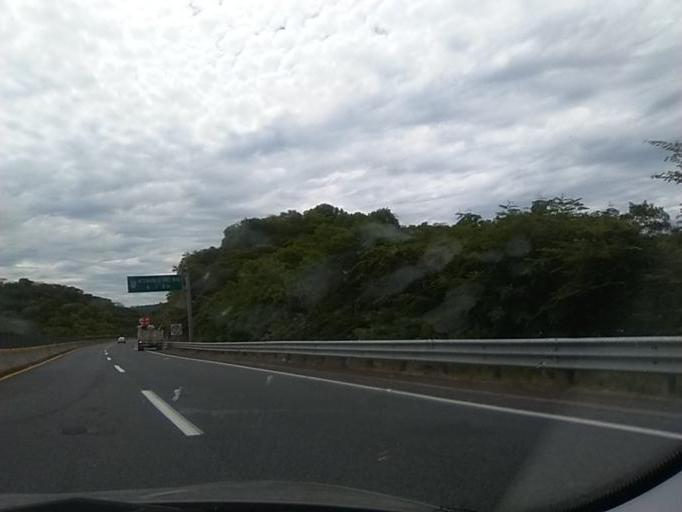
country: MX
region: Guerrero
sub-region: Huitzuco de los Figueroa
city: Ciudad de Huitzuco
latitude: 18.2440
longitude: -99.2136
